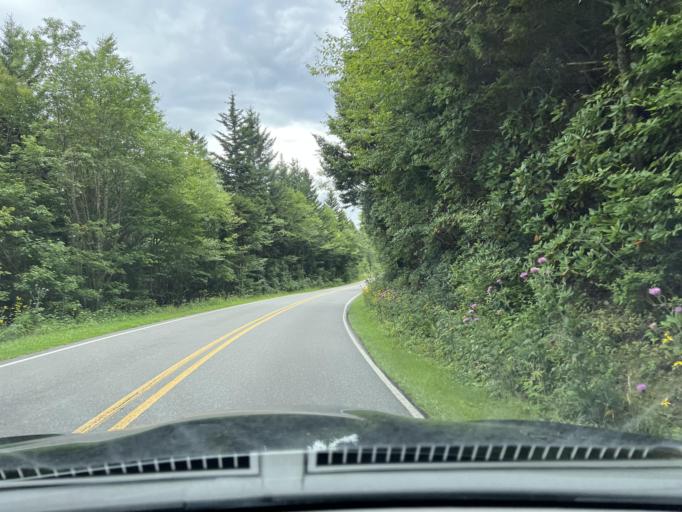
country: US
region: North Carolina
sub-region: Buncombe County
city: Black Mountain
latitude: 35.7258
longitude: -82.2831
